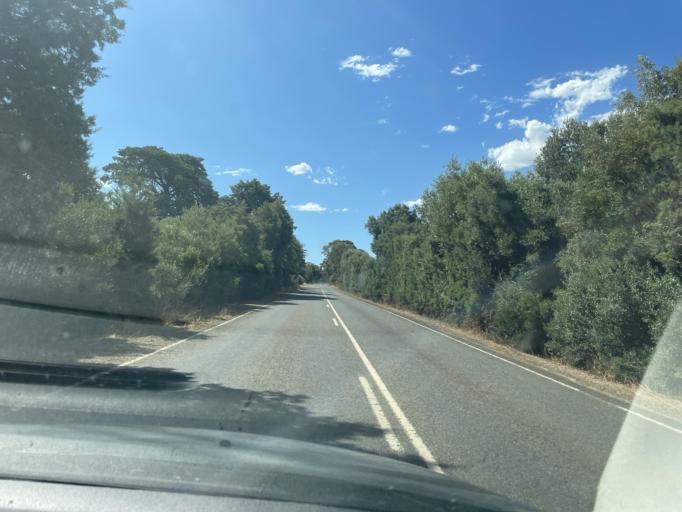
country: AU
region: South Australia
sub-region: Clare and Gilbert Valleys
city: Clare
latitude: -33.9089
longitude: 138.7142
